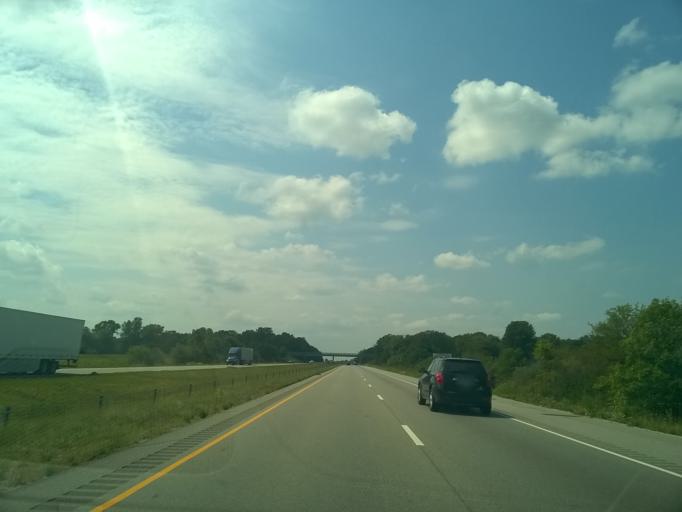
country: US
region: Indiana
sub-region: Morgan County
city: Monrovia
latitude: 39.5876
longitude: -86.5674
